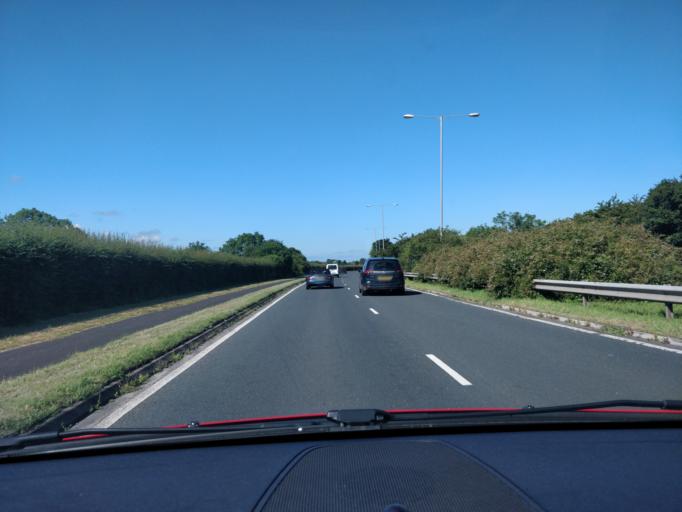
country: GB
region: England
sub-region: Lancashire
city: Tarleton
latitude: 53.6652
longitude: -2.8683
